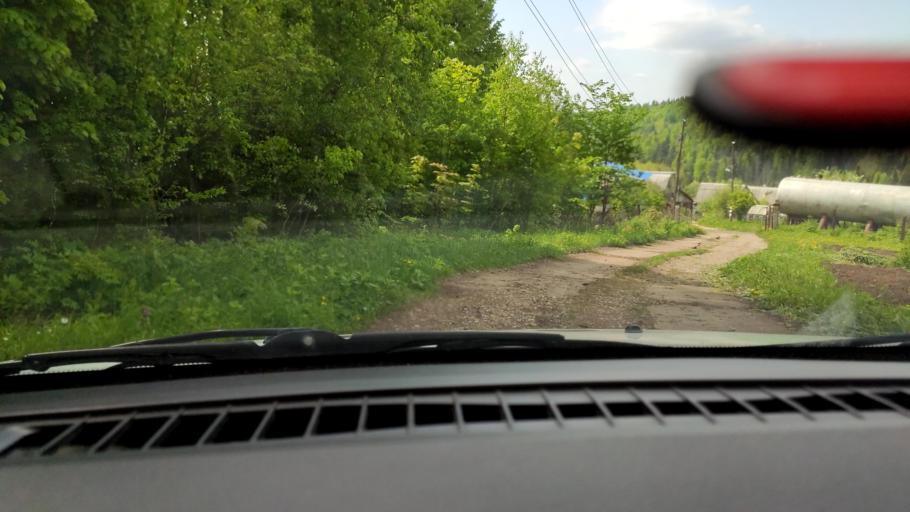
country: RU
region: Perm
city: Bershet'
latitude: 57.7219
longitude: 56.4138
